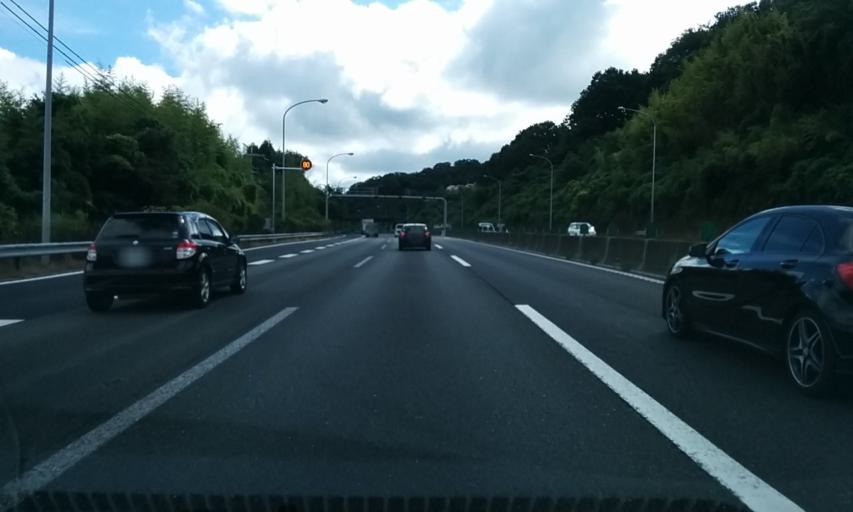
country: JP
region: Hyogo
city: Sandacho
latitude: 34.8376
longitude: 135.2495
